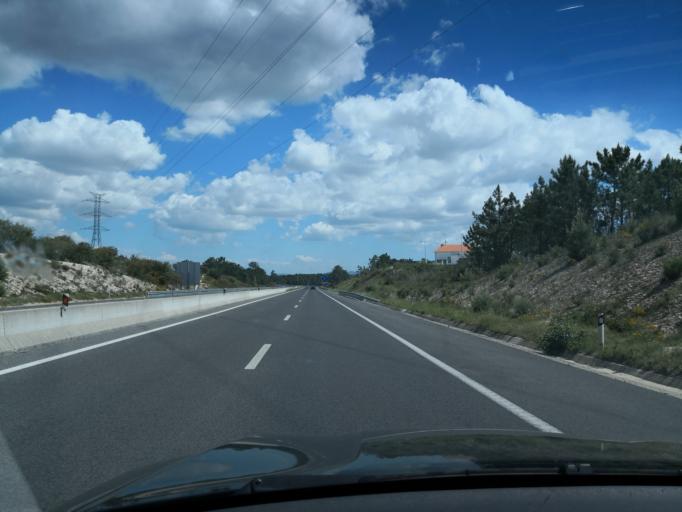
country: PT
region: Setubal
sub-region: Seixal
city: Corroios
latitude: 38.6108
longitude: -9.1536
